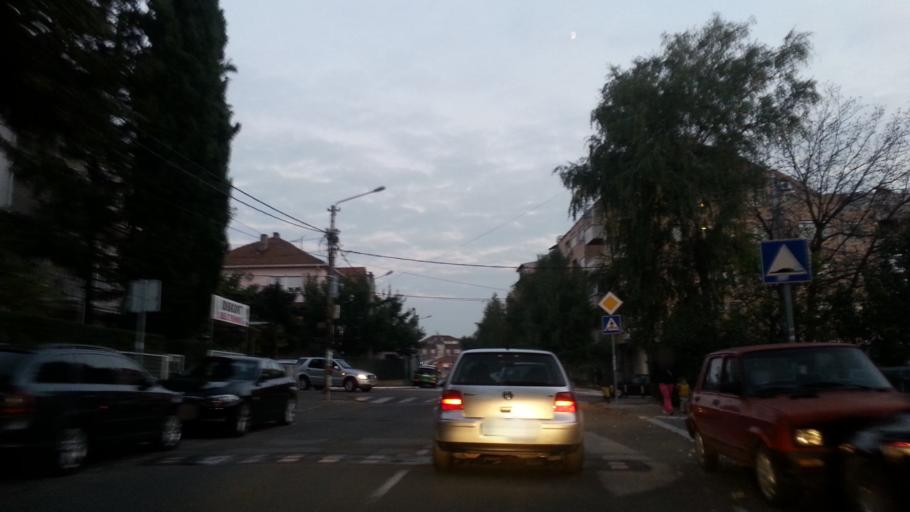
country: RS
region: Central Serbia
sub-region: Belgrade
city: Cukarica
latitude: 44.7604
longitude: 20.4194
